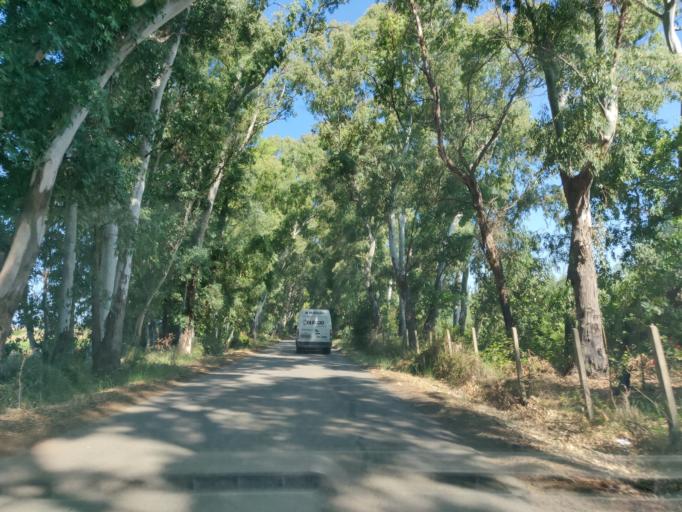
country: IT
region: Latium
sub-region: Citta metropolitana di Roma Capitale
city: Aurelia
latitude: 42.1617
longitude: 11.7467
